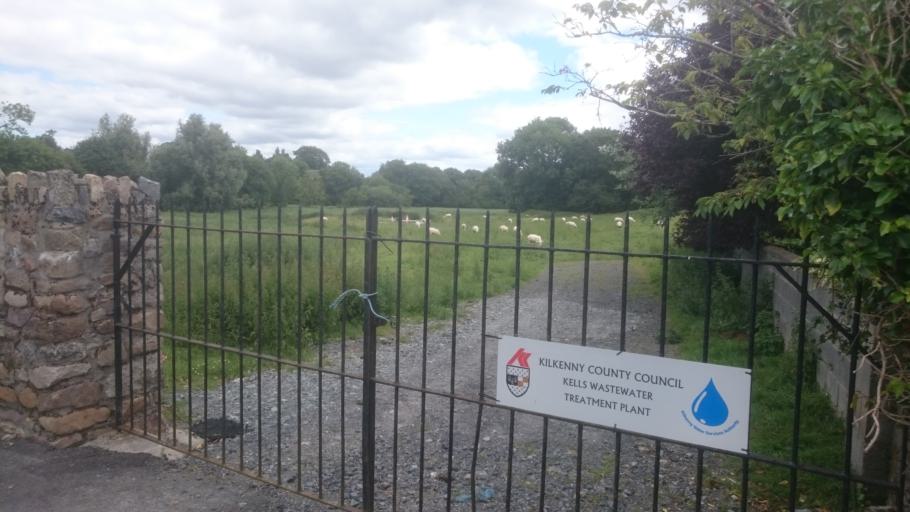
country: IE
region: Leinster
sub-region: Kilkenny
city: Kilkenny
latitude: 52.5403
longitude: -7.2727
